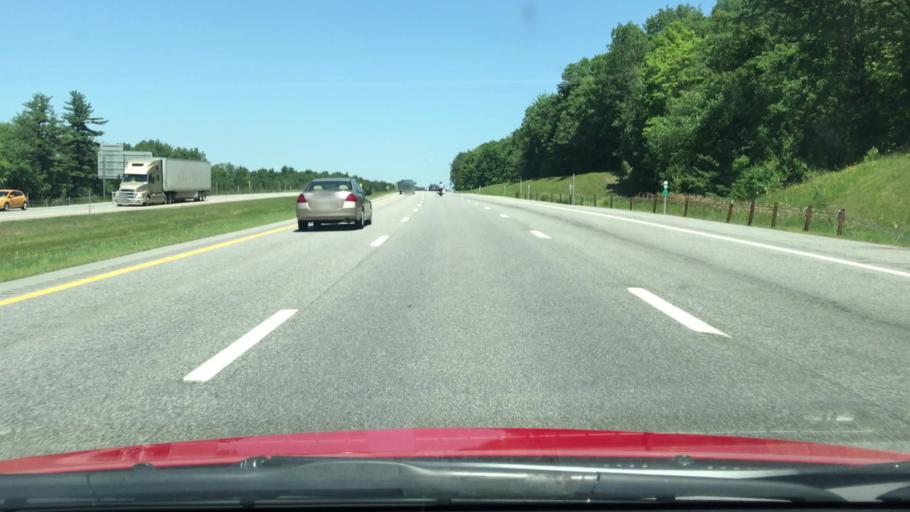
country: US
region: New York
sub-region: Essex County
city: Keeseville
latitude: 44.4479
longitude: -73.4895
